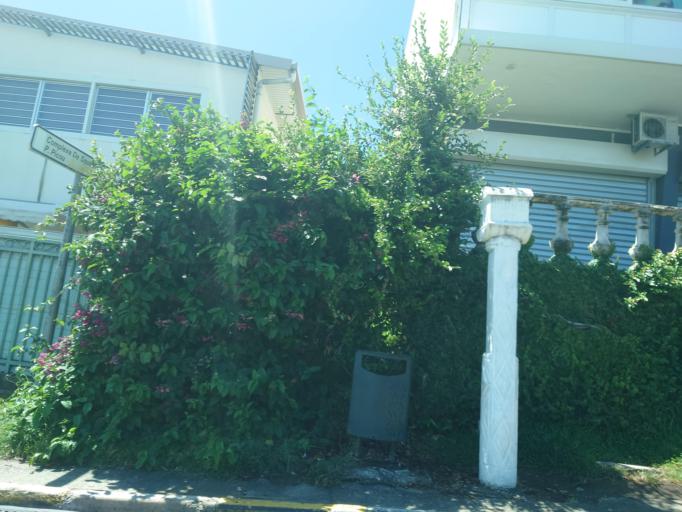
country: NC
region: South Province
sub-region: Noumea
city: Noumea
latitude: -22.2714
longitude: 166.4519
